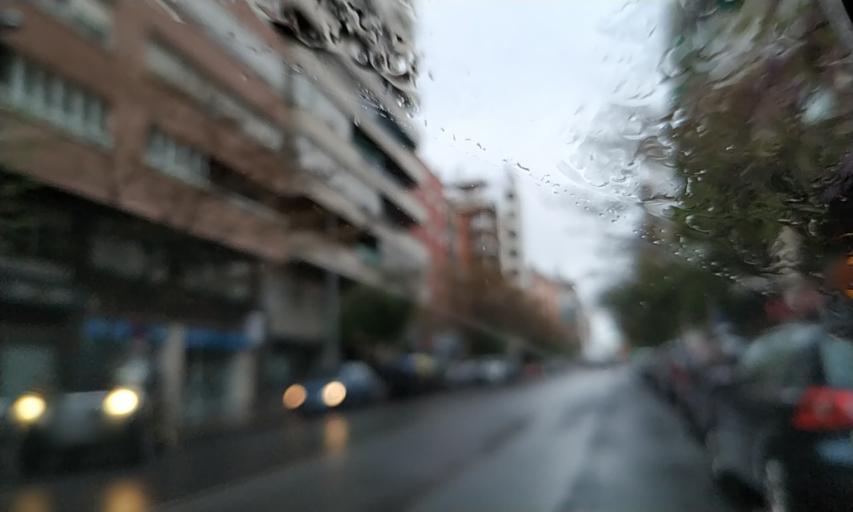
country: ES
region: Extremadura
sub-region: Provincia de Badajoz
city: Badajoz
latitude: 38.8745
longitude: -6.9727
